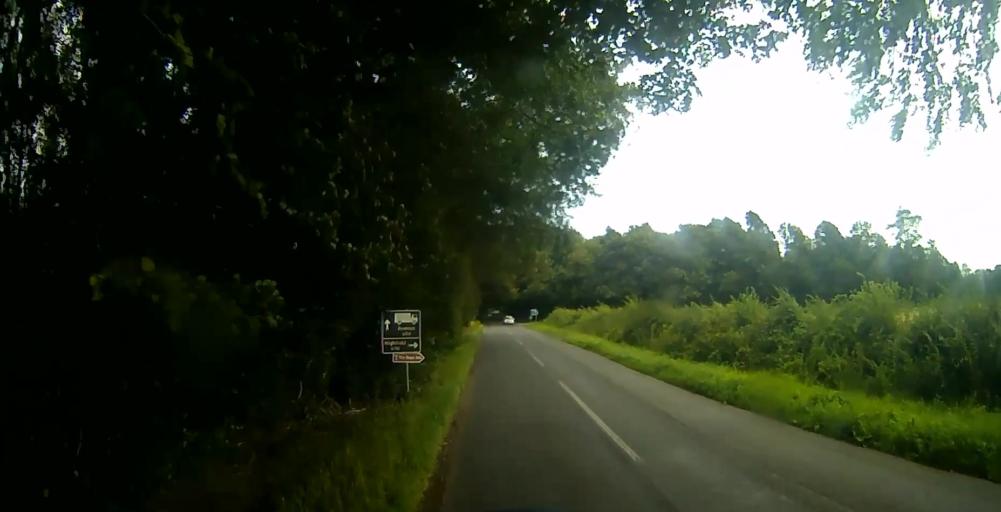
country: GB
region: England
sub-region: Hampshire
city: Alton
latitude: 51.1900
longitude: -1.0198
